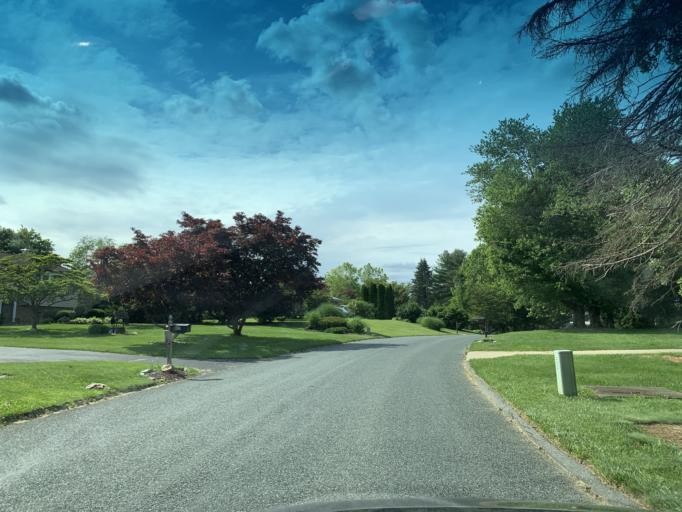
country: US
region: Maryland
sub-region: Harford County
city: Jarrettsville
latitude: 39.6044
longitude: -76.4680
